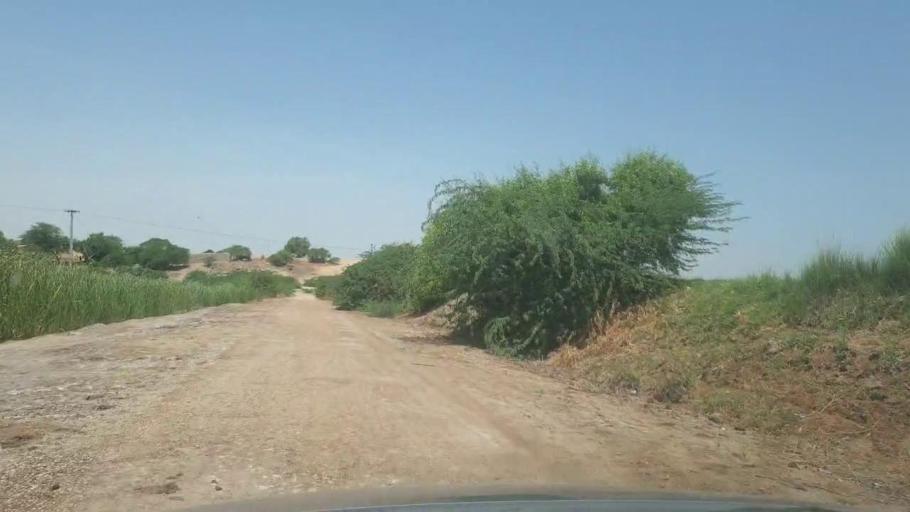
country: PK
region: Sindh
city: Kot Diji
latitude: 27.3251
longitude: 69.0132
